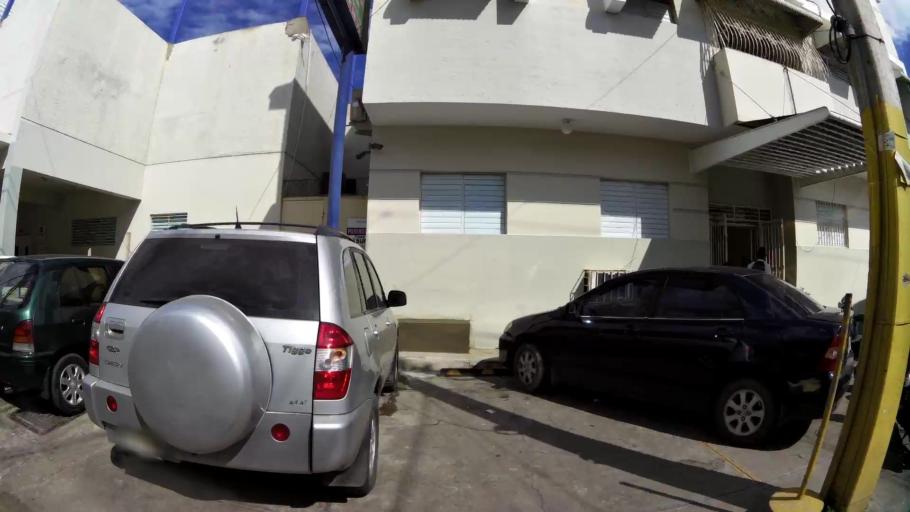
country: DO
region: La Vega
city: Concepcion de La Vega
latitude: 19.2243
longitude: -70.5270
